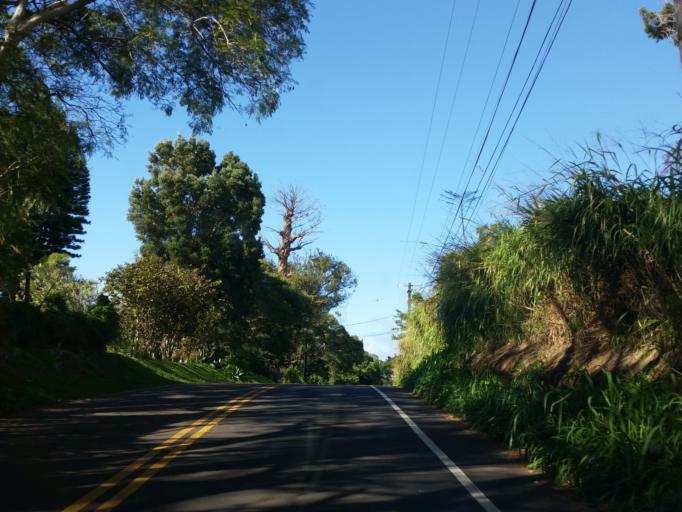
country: US
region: Hawaii
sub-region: Maui County
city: Makawao
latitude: 20.8357
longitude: -156.3115
